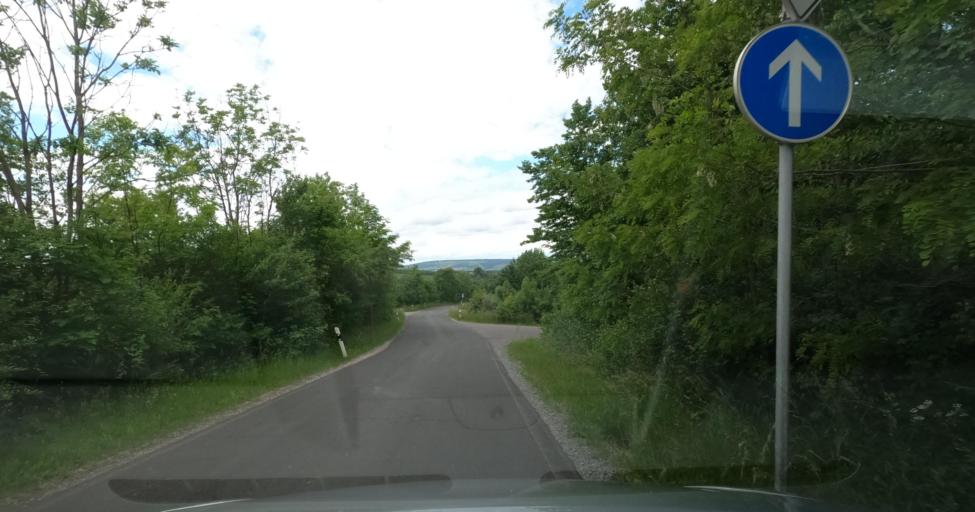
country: DE
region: Thuringia
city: Vollersroda
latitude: 50.9475
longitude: 11.3458
